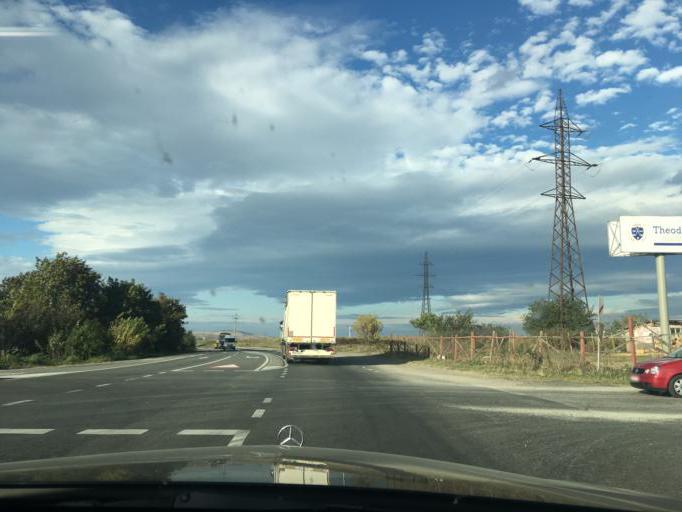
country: RO
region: Alba
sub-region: Municipiul Alba Iulia
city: Alba Iulia
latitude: 46.0707
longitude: 23.5956
